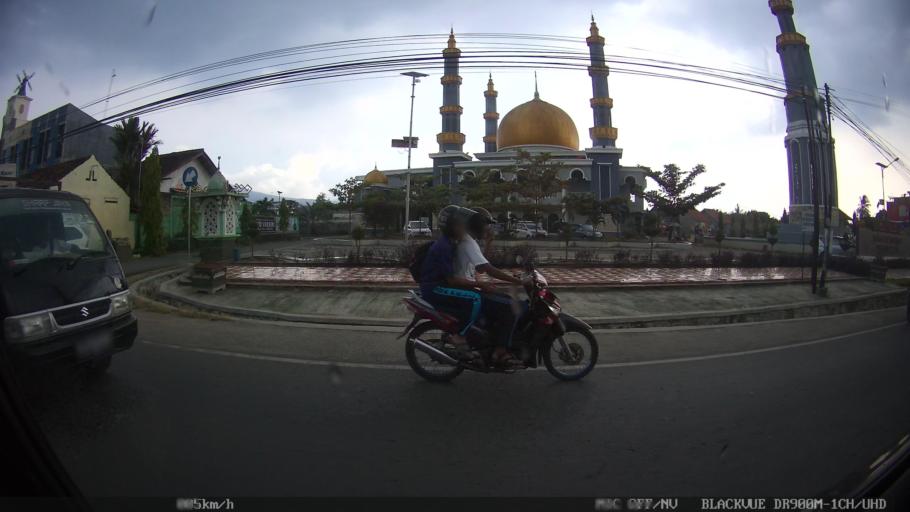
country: ID
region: Lampung
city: Gedongtataan
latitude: -5.3799
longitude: 105.1063
